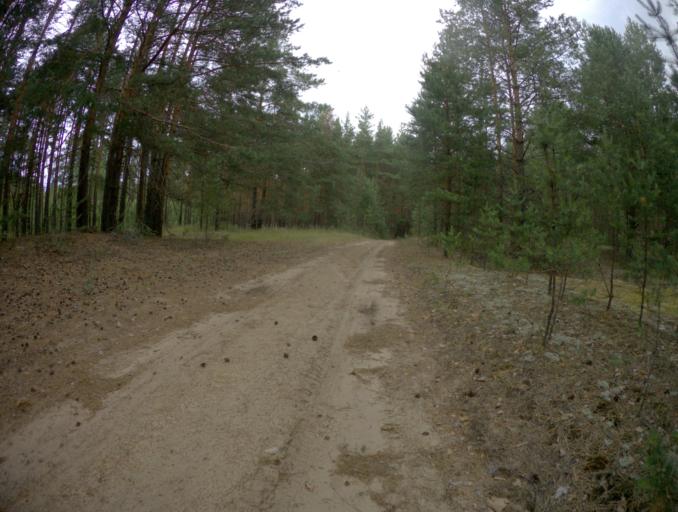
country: RU
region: Vladimir
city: Gorokhovets
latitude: 56.3194
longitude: 42.7340
